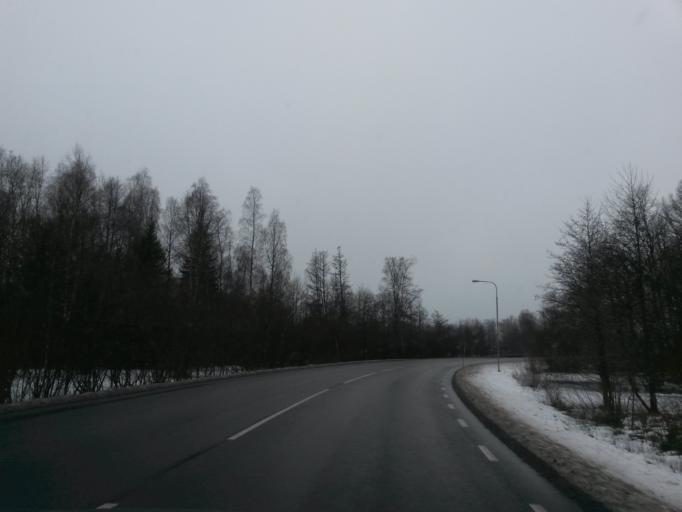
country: SE
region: Vaestra Goetaland
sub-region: Tranemo Kommun
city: Langhem
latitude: 57.6754
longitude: 13.3297
